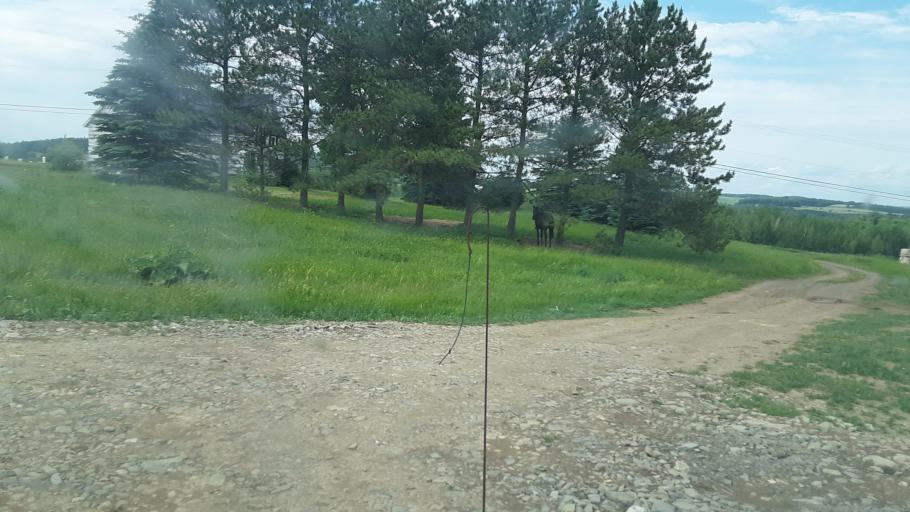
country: US
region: Maine
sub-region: Aroostook County
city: Fort Fairfield
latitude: 46.7565
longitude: -67.8633
